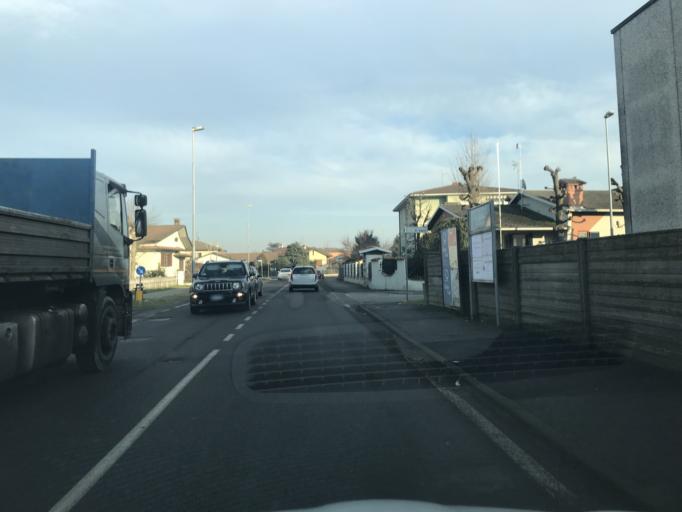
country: IT
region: Lombardy
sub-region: Provincia di Lodi
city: Borgo San Giovanni
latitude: 45.2763
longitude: 9.4293
